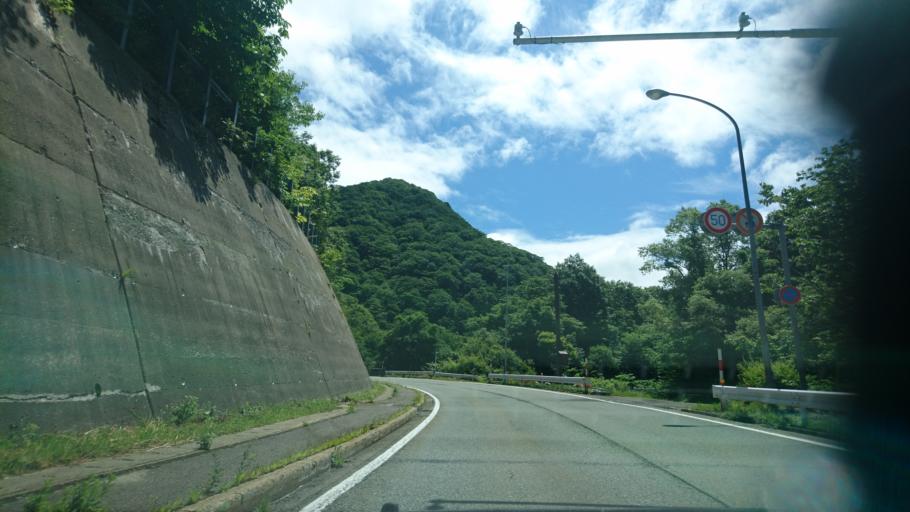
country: JP
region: Iwate
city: Shizukuishi
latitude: 39.6935
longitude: 140.7818
